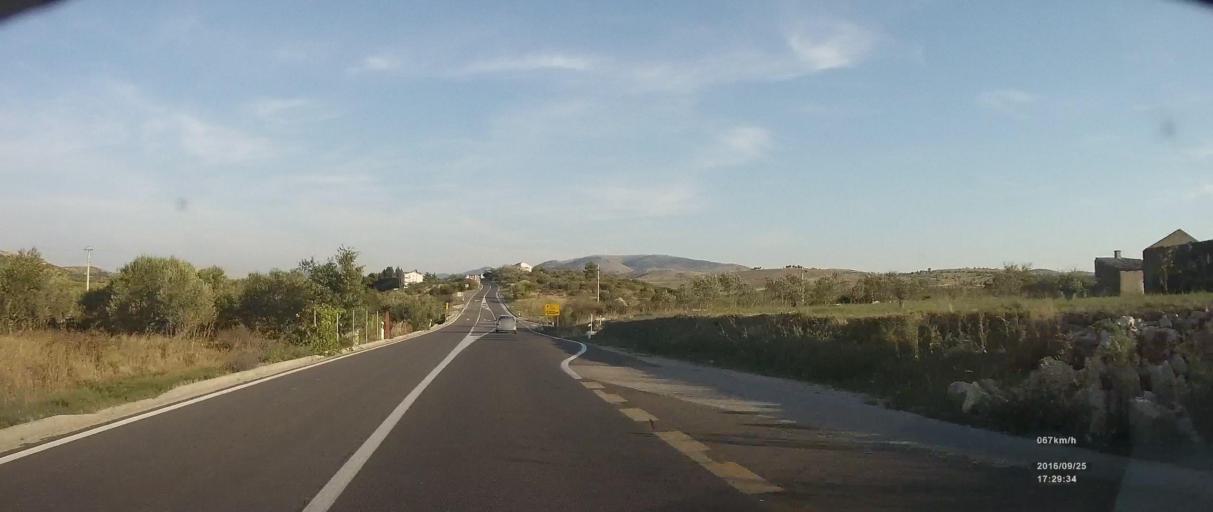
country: HR
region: Sibensko-Kniniska
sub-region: Grad Sibenik
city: Brodarica
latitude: 43.6855
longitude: 15.9669
